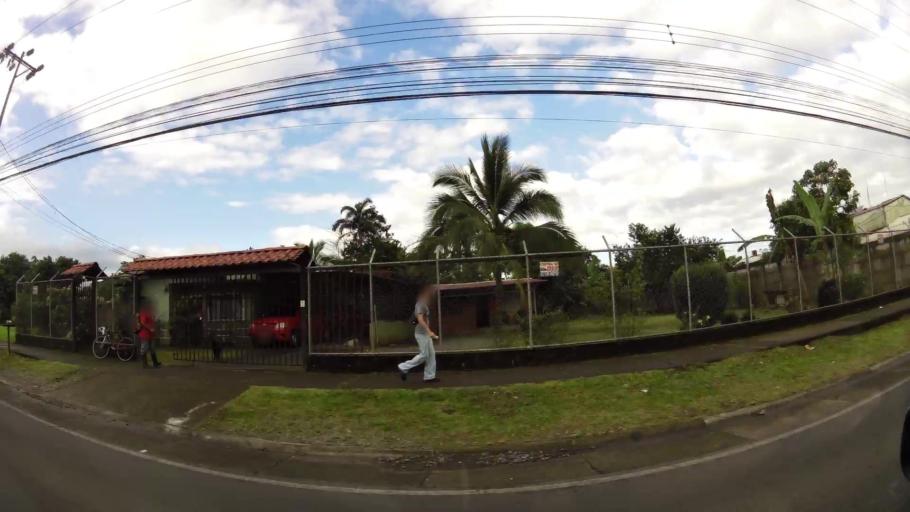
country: CR
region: Limon
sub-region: Canton de Pococi
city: Guapiles
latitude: 10.2086
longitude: -83.7960
